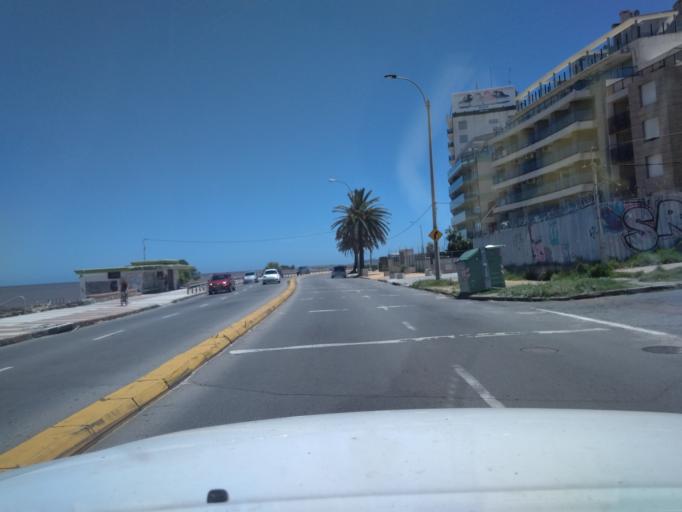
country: UY
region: Canelones
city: Paso de Carrasco
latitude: -34.8962
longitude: -56.0952
